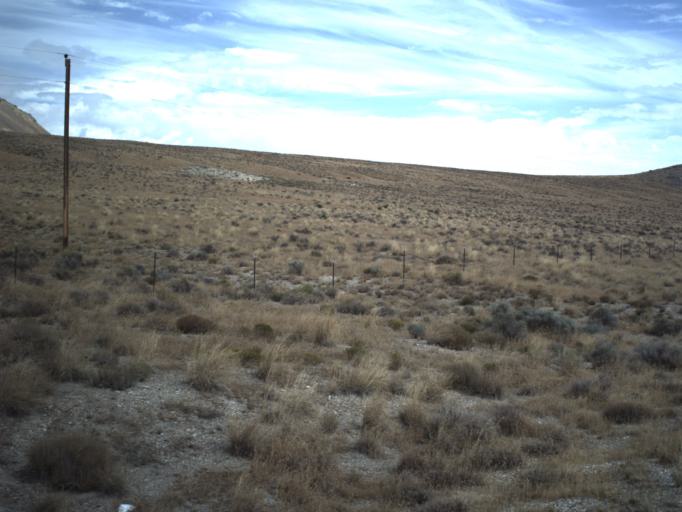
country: US
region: Utah
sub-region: Tooele County
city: Wendover
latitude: 41.4531
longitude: -113.6647
